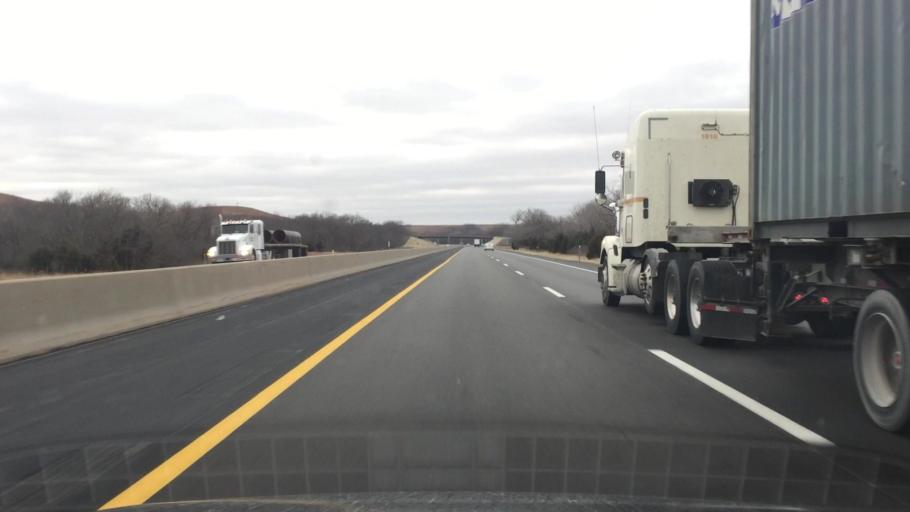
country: US
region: Kansas
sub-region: Chase County
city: Cottonwood Falls
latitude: 38.1444
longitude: -96.5156
